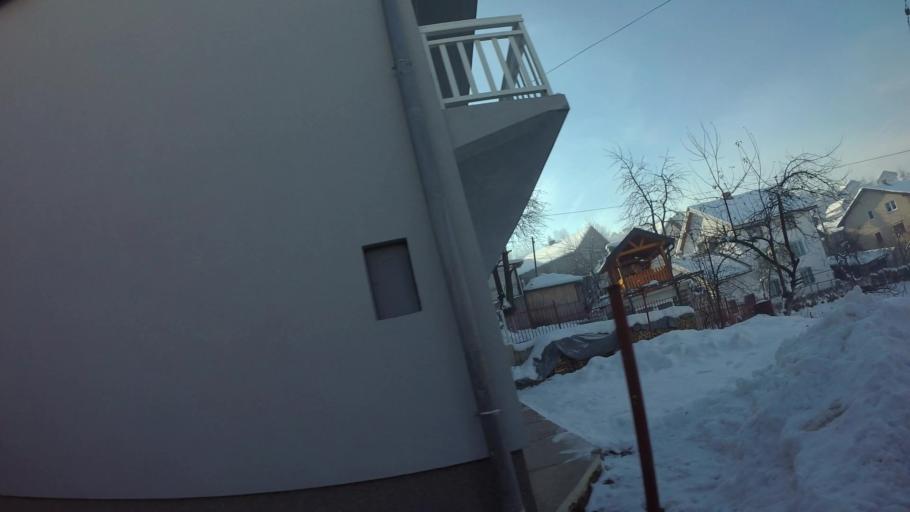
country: BA
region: Federation of Bosnia and Herzegovina
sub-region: Kanton Sarajevo
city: Sarajevo
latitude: 43.8395
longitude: 18.3639
